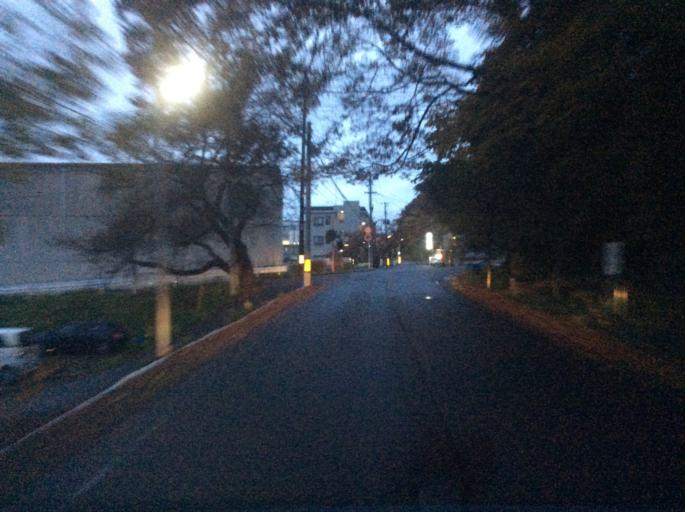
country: JP
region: Fukushima
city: Iwaki
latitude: 37.0614
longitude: 140.8932
